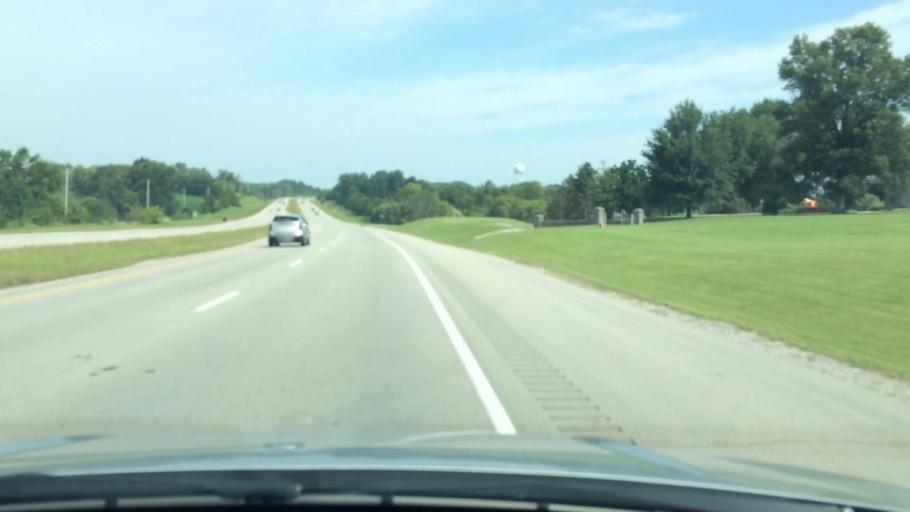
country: US
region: Kentucky
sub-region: Anderson County
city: Lawrenceburg
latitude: 38.1120
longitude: -84.9141
